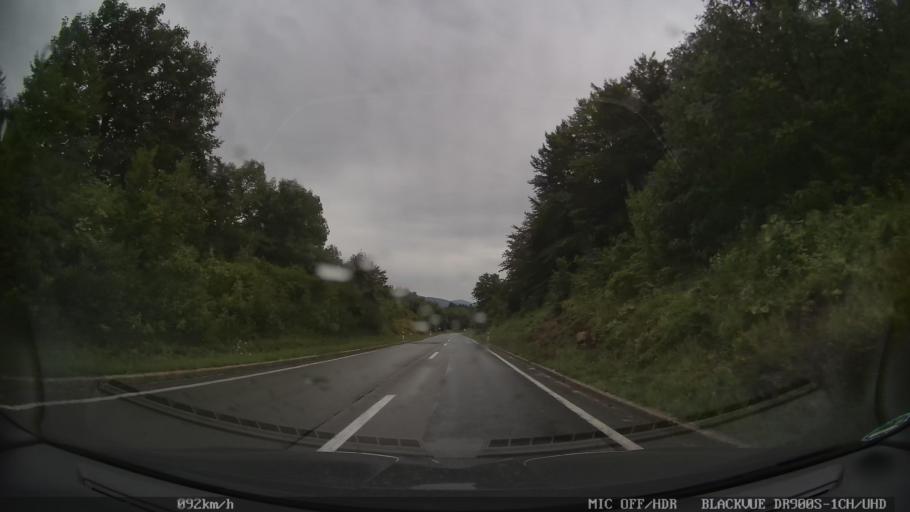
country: HR
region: Licko-Senjska
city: Brinje
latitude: 44.9625
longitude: 15.0853
